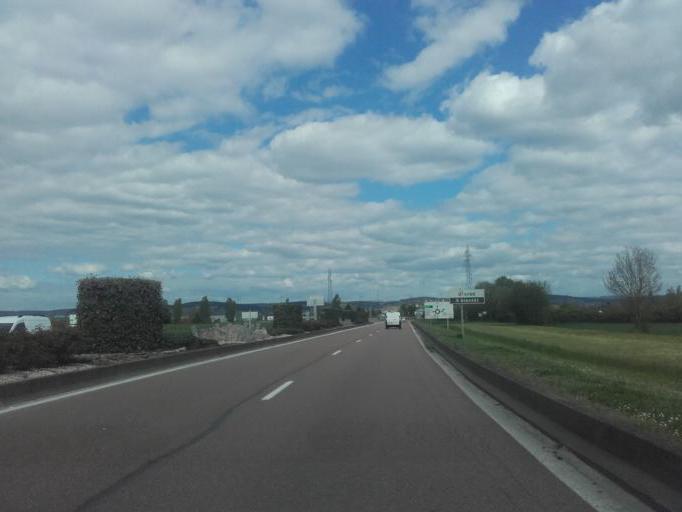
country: FR
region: Bourgogne
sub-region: Departement de la Cote-d'Or
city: Bligny-les-Beaune
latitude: 47.0036
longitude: 4.8530
